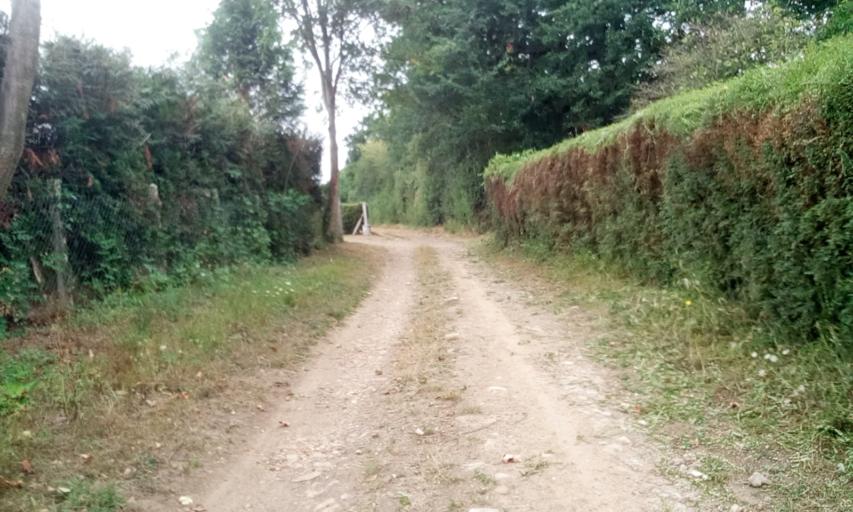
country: FR
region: Lower Normandy
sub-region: Departement du Calvados
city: Eterville
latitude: 49.1561
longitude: -0.4354
